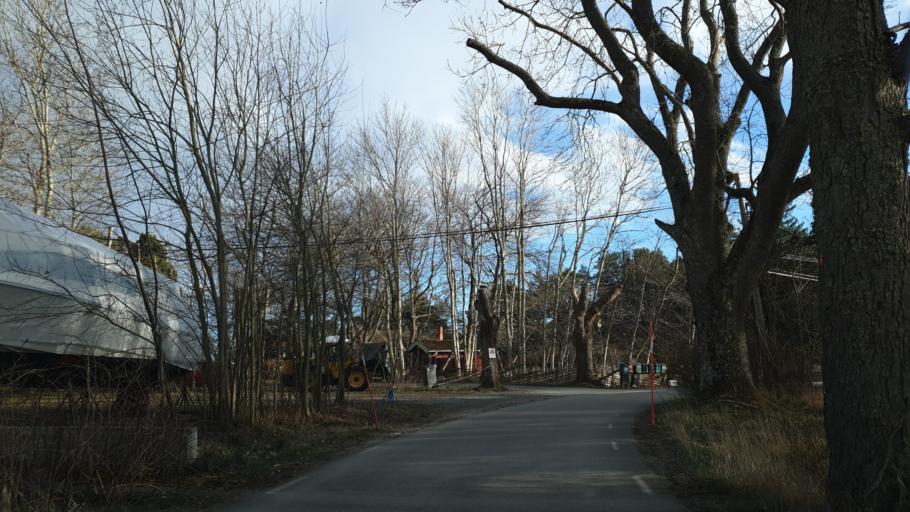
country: SE
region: Stockholm
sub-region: Varmdo Kommun
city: Holo
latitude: 59.3076
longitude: 18.6917
